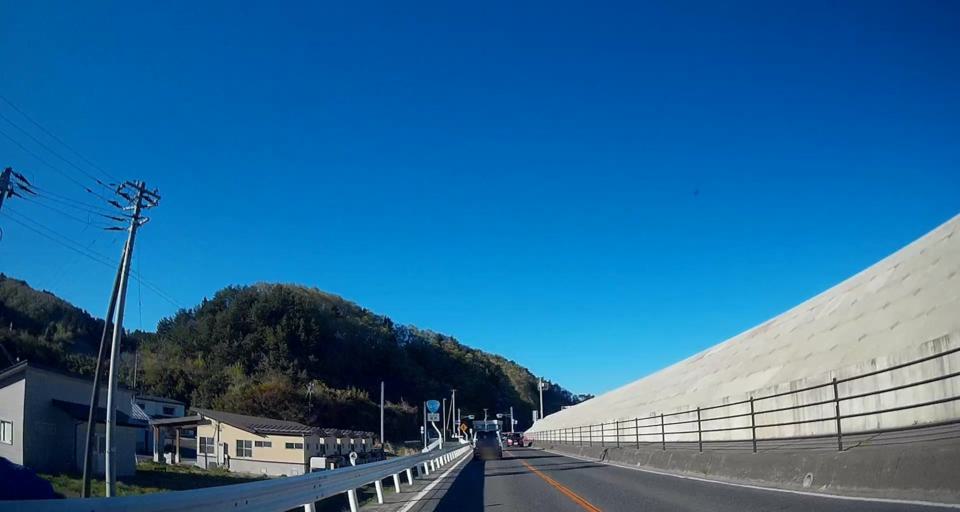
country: JP
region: Iwate
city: Miyako
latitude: 39.6072
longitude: 141.9570
